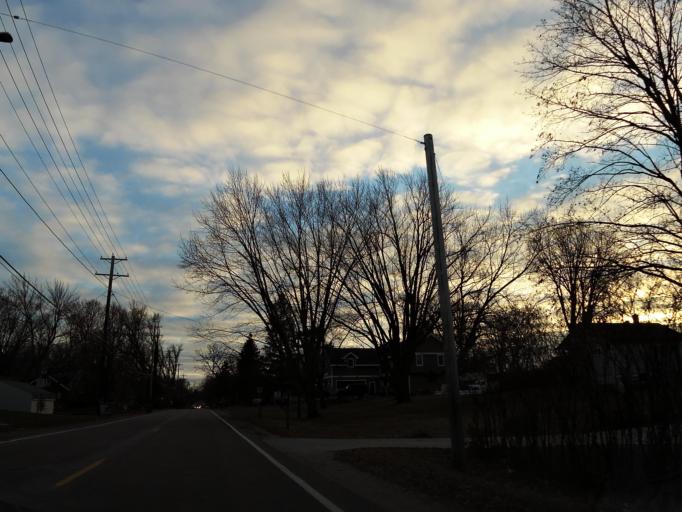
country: US
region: Minnesota
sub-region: Washington County
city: Mahtomedi
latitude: 45.0621
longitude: -92.9584
